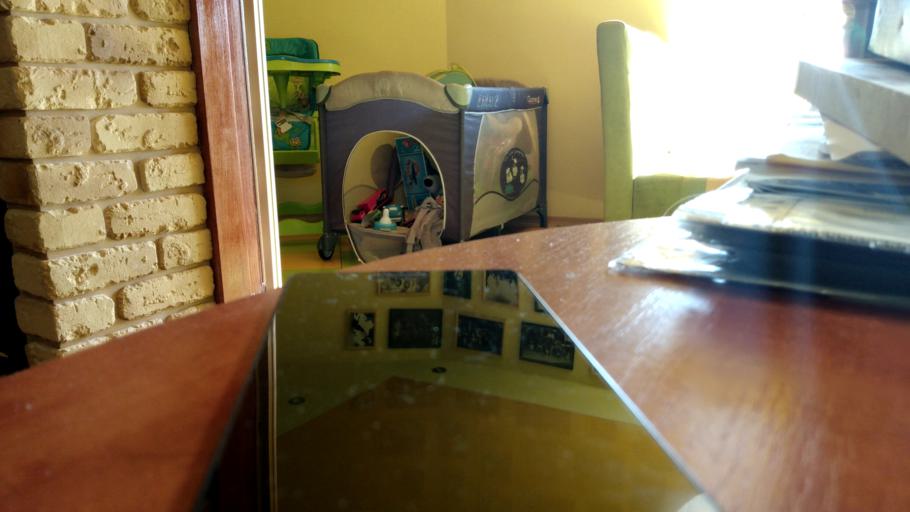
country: RU
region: Penza
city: Serdobsk
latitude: 52.3362
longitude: 44.3726
